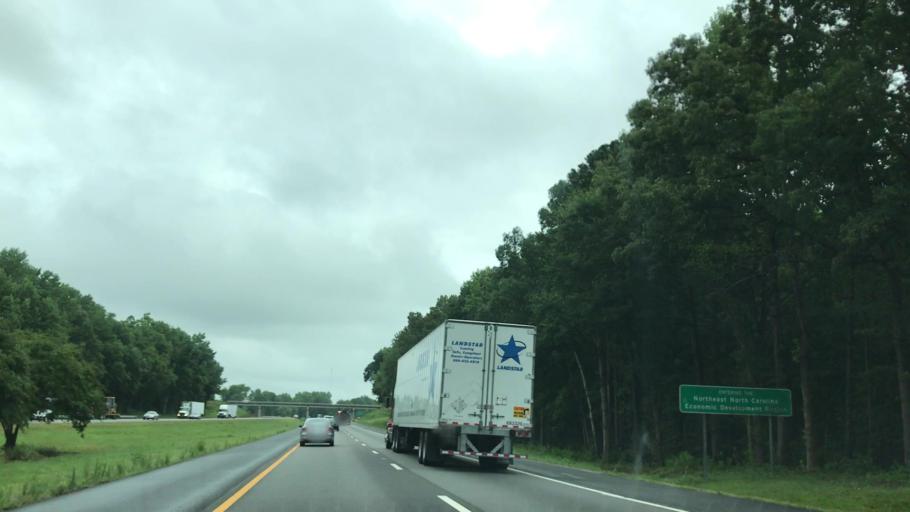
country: US
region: North Carolina
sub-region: Halifax County
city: Enfield
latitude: 36.1530
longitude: -77.7838
